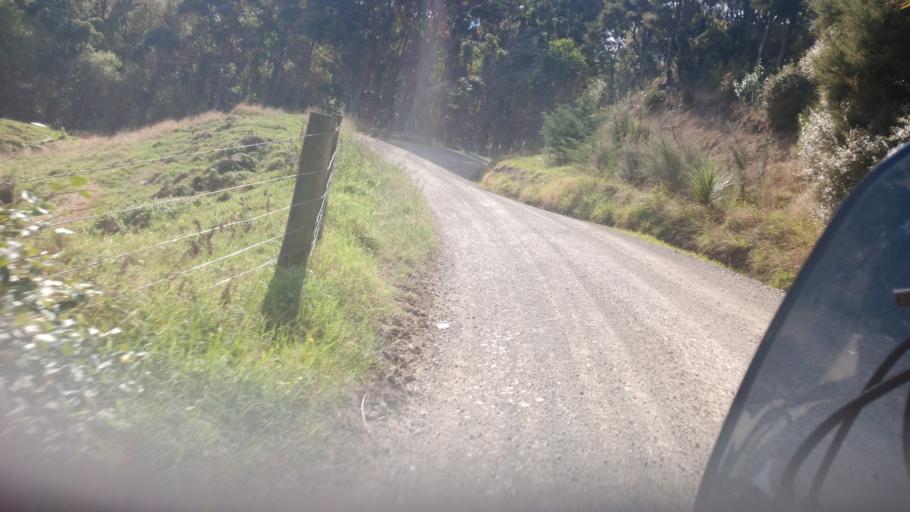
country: NZ
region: Gisborne
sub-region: Gisborne District
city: Gisborne
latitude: -38.4028
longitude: 177.6798
